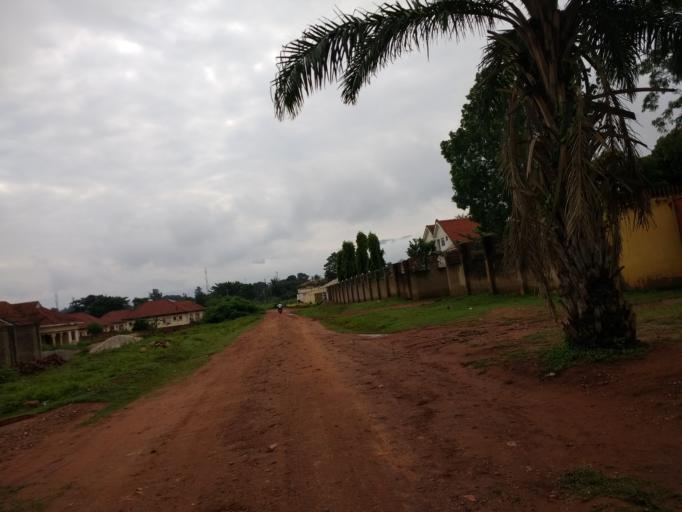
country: UG
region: Eastern Region
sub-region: Mbale District
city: Mbale
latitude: 1.0701
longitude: 34.1653
